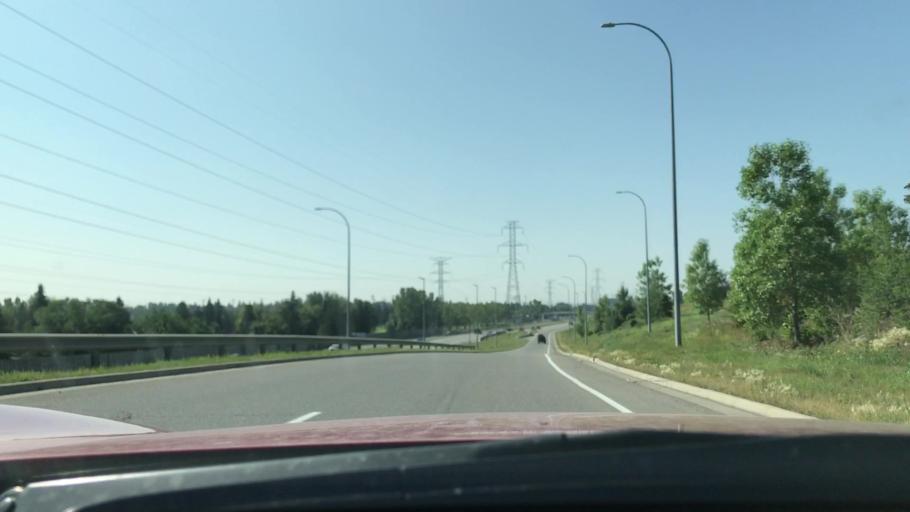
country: CA
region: Alberta
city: Calgary
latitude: 51.0381
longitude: -114.1653
